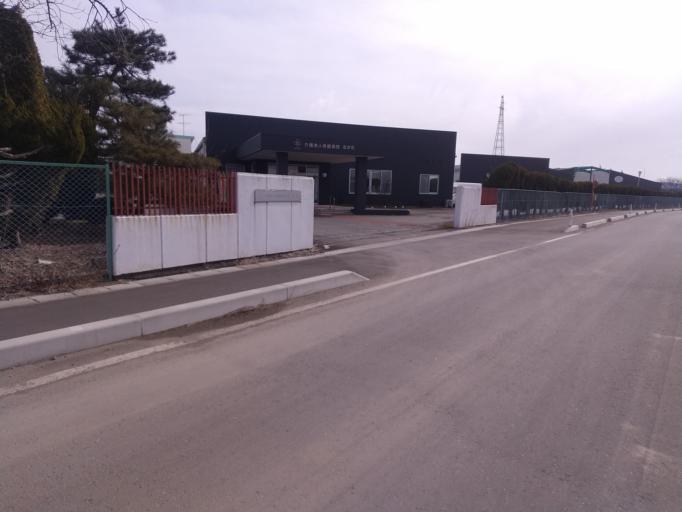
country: JP
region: Miyagi
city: Wakuya
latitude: 38.7164
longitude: 141.2610
